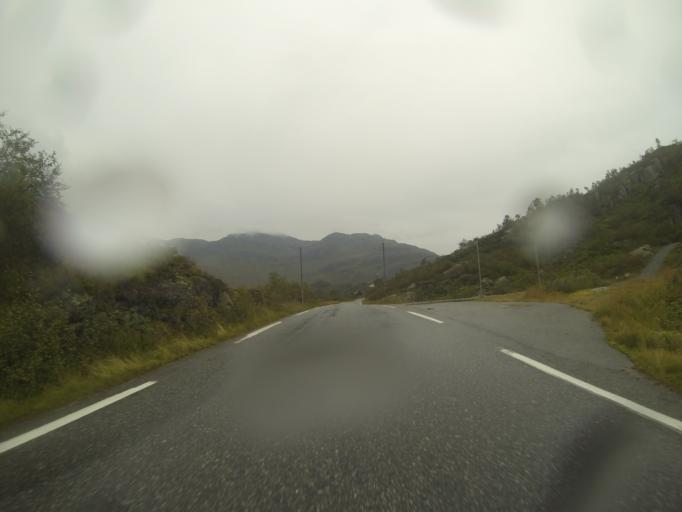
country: NO
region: Rogaland
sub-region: Sauda
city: Sauda
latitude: 59.7258
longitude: 6.5777
